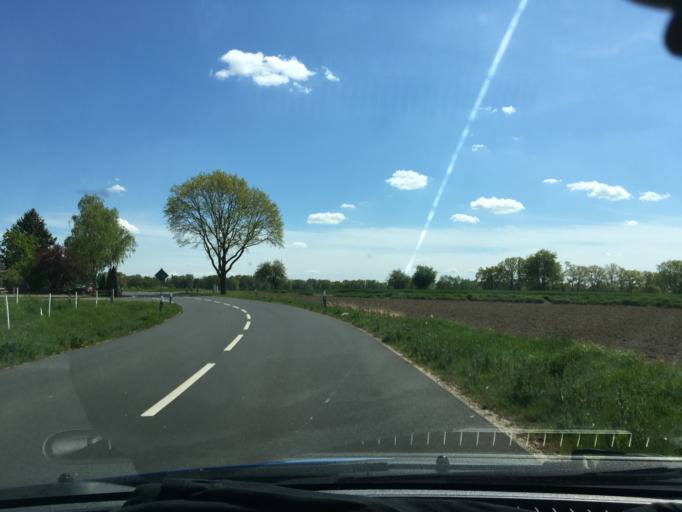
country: DE
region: Lower Saxony
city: Stoetze
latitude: 53.0716
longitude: 10.7700
